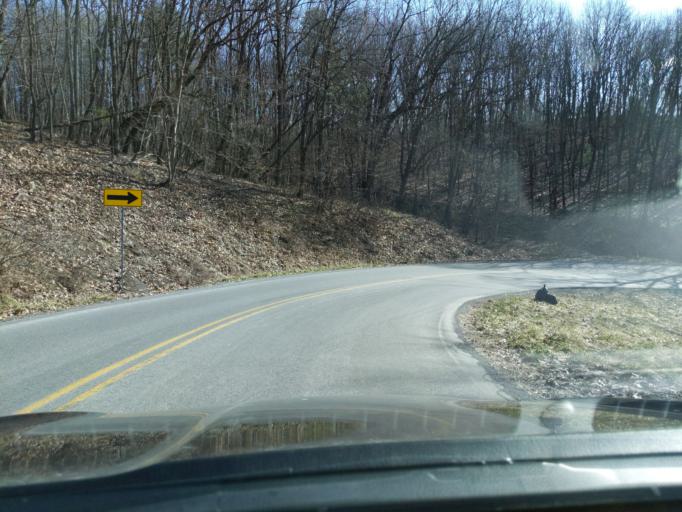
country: US
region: Pennsylvania
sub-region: Blair County
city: Williamsburg
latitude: 40.4212
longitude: -78.2873
